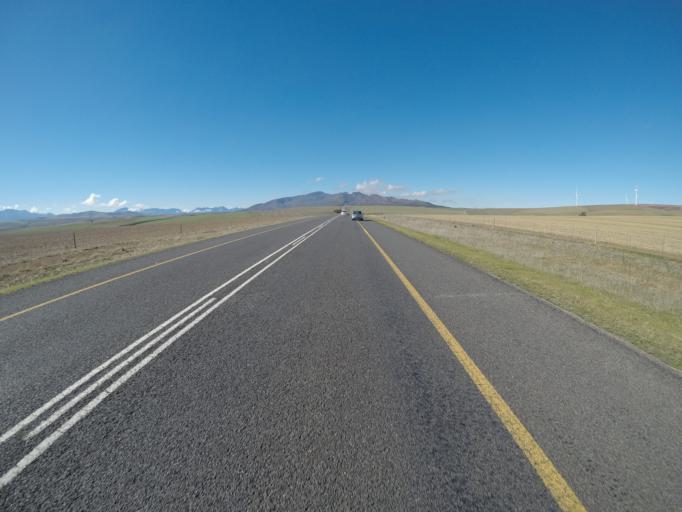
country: ZA
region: Western Cape
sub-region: Overberg District Municipality
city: Caledon
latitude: -34.2115
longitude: 19.3649
